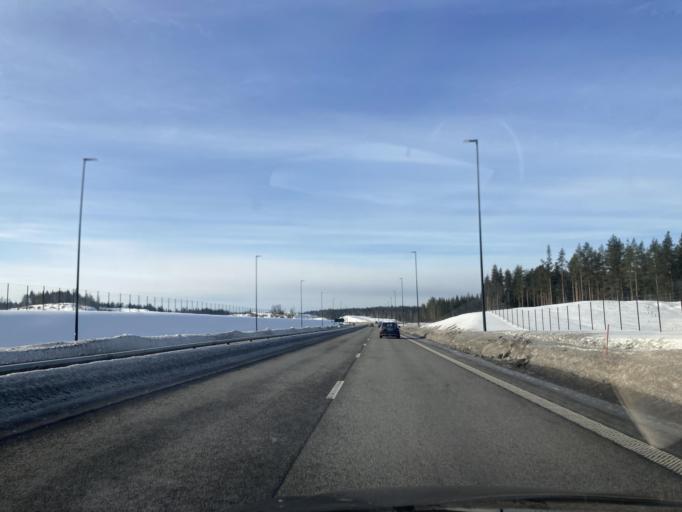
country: NO
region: Hedmark
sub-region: Elverum
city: Elverum
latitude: 60.8831
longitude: 11.4908
